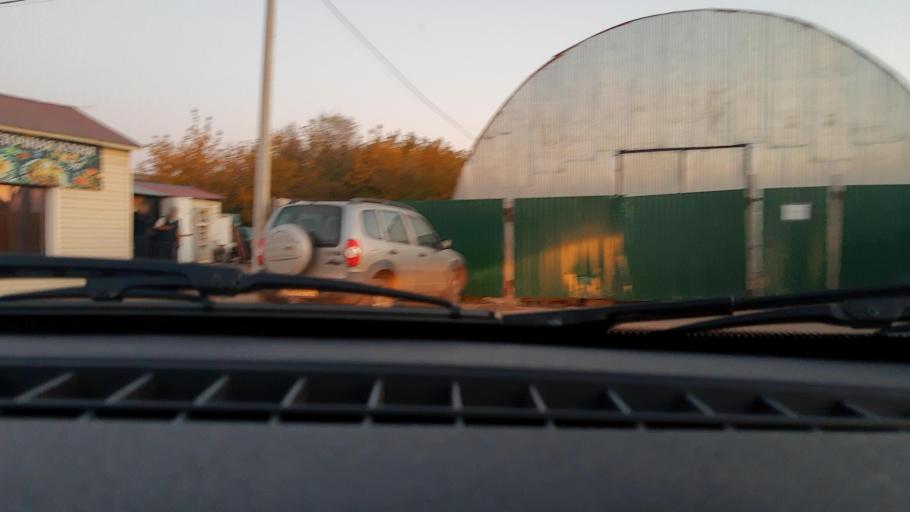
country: RU
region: Bashkortostan
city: Ufa
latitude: 54.7682
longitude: 55.9597
